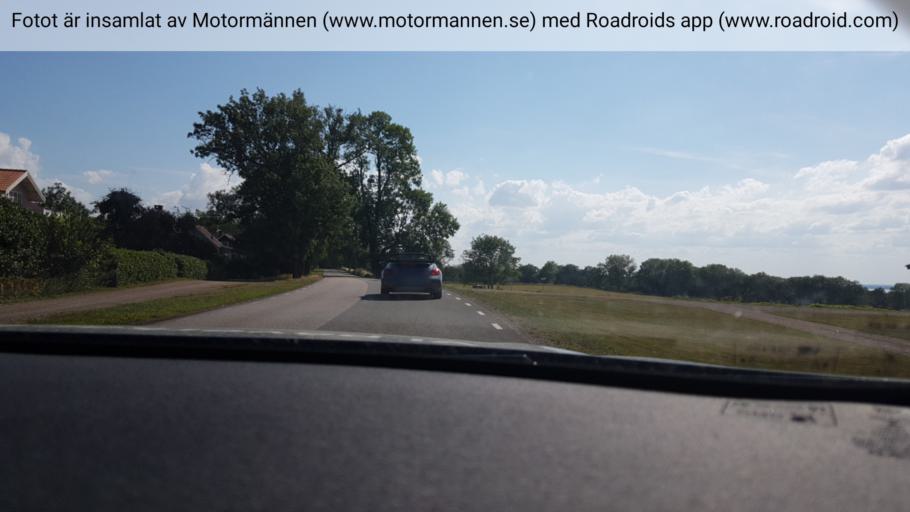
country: SE
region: Vaestra Goetaland
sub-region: Gotene Kommun
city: Kallby
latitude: 58.5470
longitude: 13.3319
